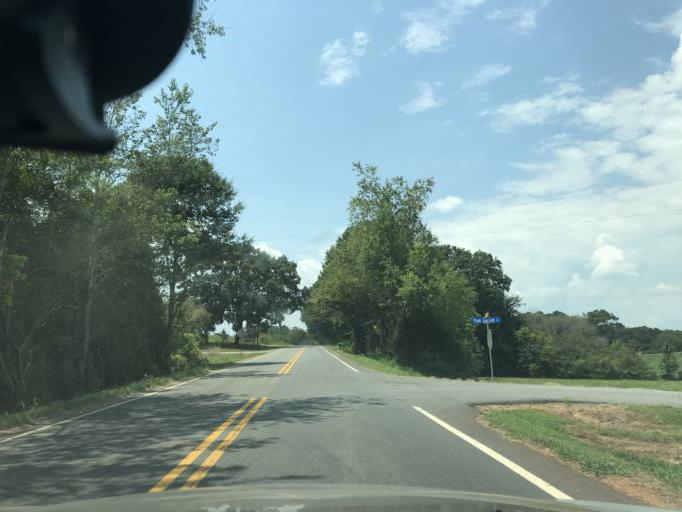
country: US
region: Georgia
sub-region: Dawson County
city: Dawsonville
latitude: 34.3378
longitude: -84.1385
